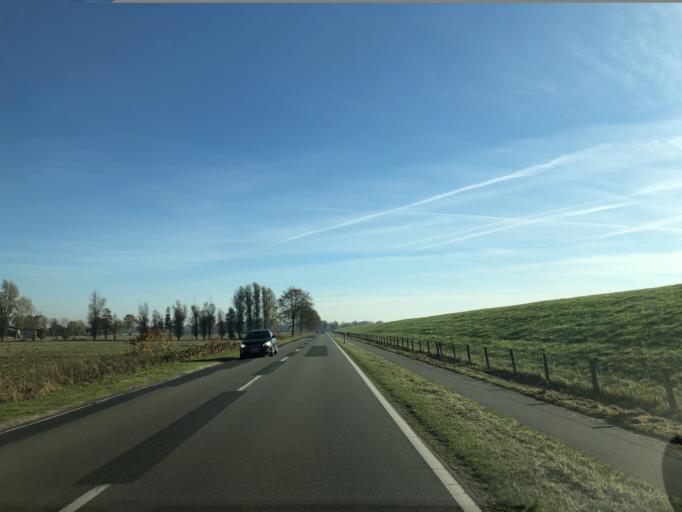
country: DE
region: Lower Saxony
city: Rhede
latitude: 53.0586
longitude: 7.3020
